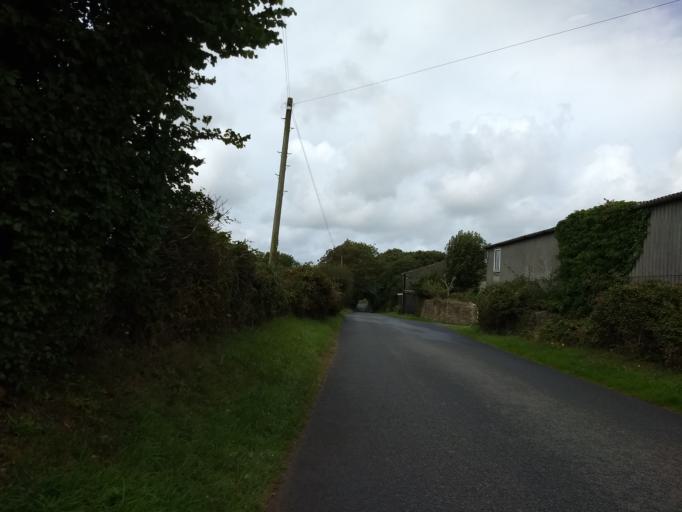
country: GB
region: England
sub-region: Isle of Wight
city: Newchurch
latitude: 50.6483
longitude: -1.2252
